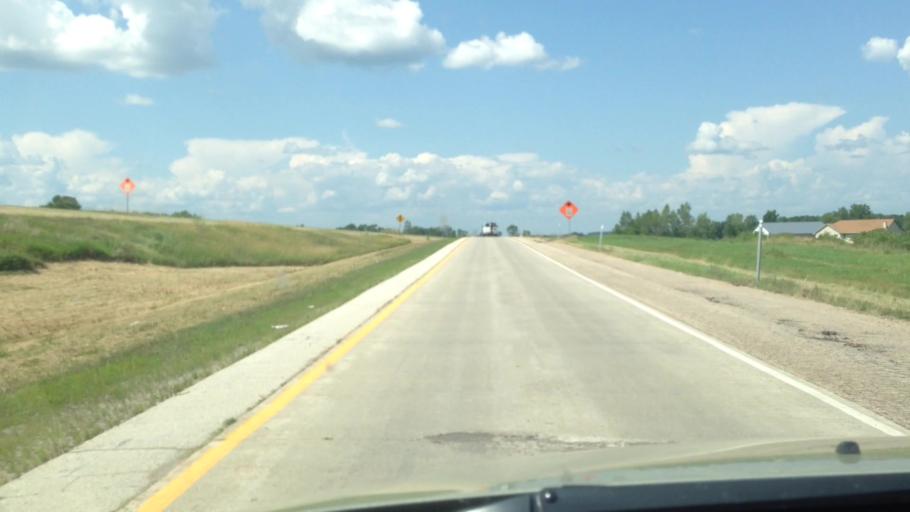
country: US
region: Wisconsin
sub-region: Brown County
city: Pulaski
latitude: 44.6746
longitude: -88.3083
